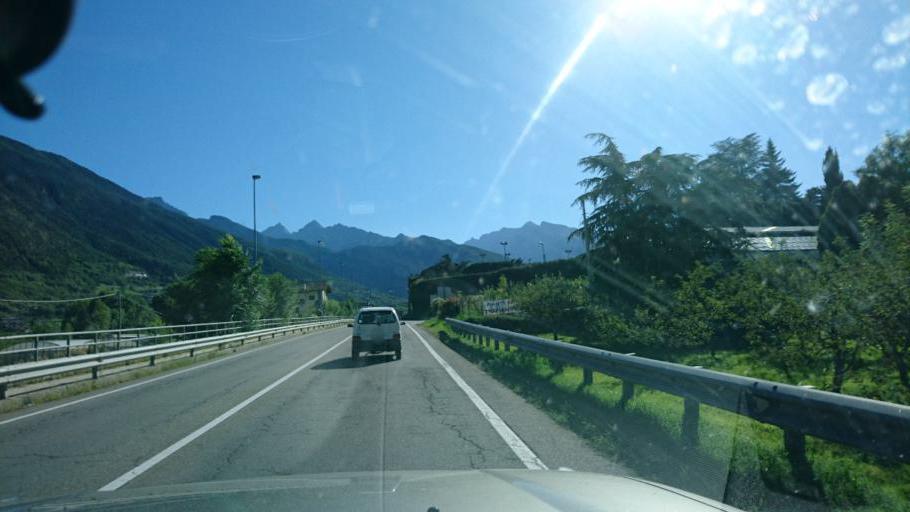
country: IT
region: Aosta Valley
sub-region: Valle d'Aosta
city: Saint Maurice
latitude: 45.7190
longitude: 7.2632
